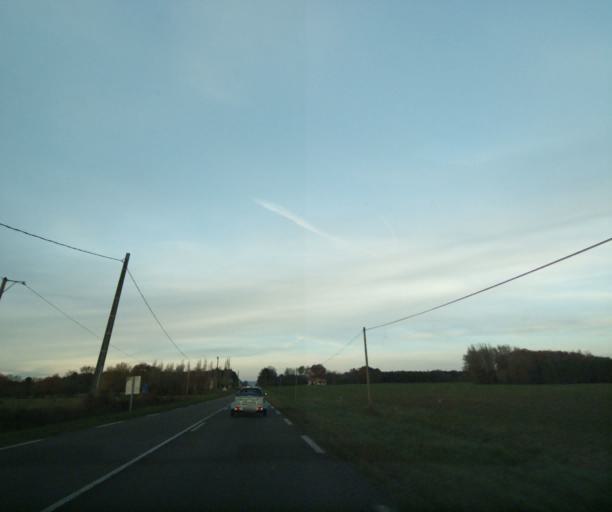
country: FR
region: Aquitaine
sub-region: Departement de la Gironde
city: Langon
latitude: 44.4995
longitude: -0.2377
